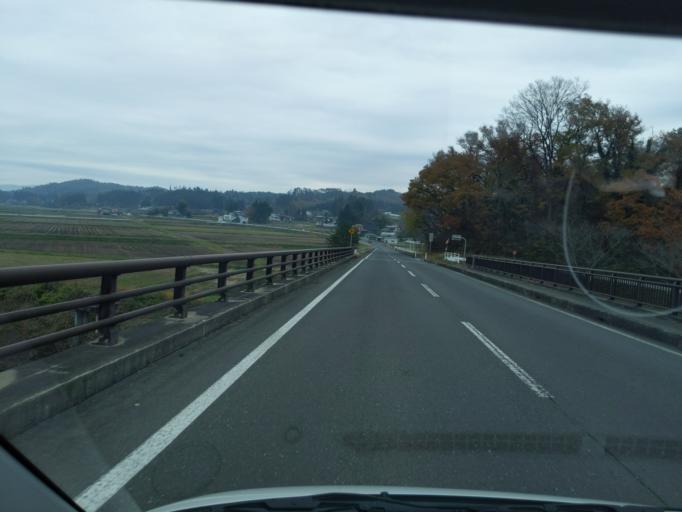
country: JP
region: Iwate
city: Mizusawa
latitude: 39.1673
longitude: 141.2078
